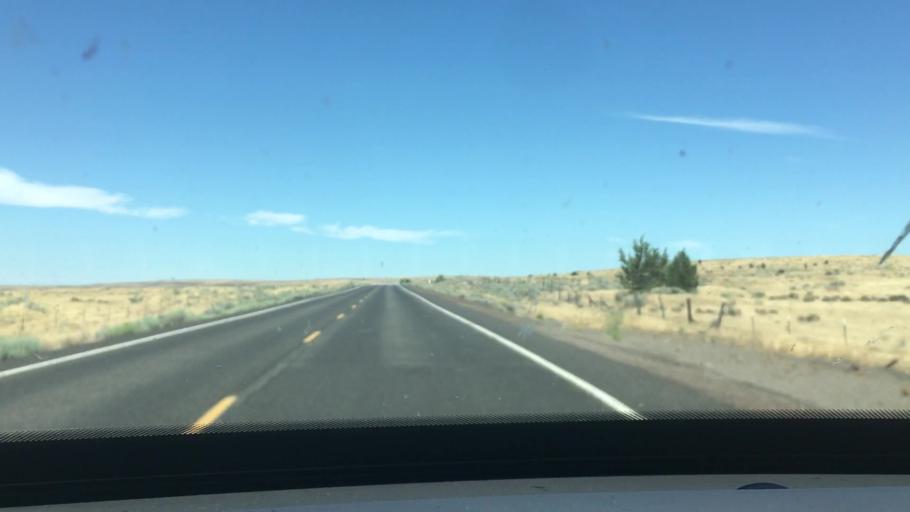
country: US
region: Oregon
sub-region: Jefferson County
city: Madras
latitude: 44.9595
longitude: -120.8902
